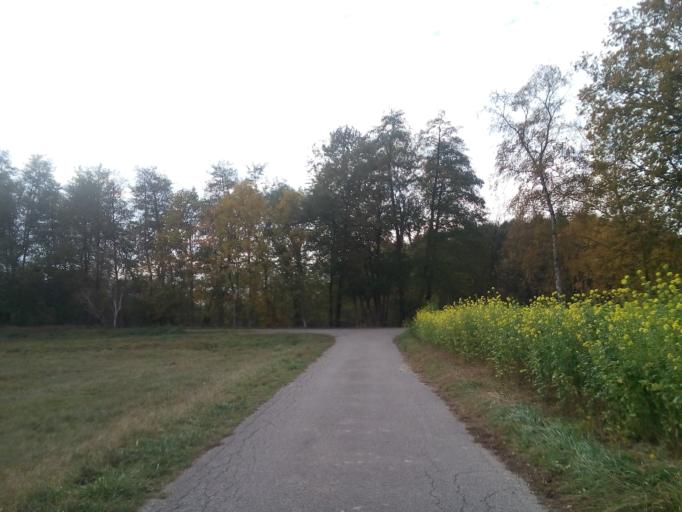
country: DE
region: Baden-Wuerttemberg
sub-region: Karlsruhe Region
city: Zell
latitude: 48.6723
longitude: 8.0475
